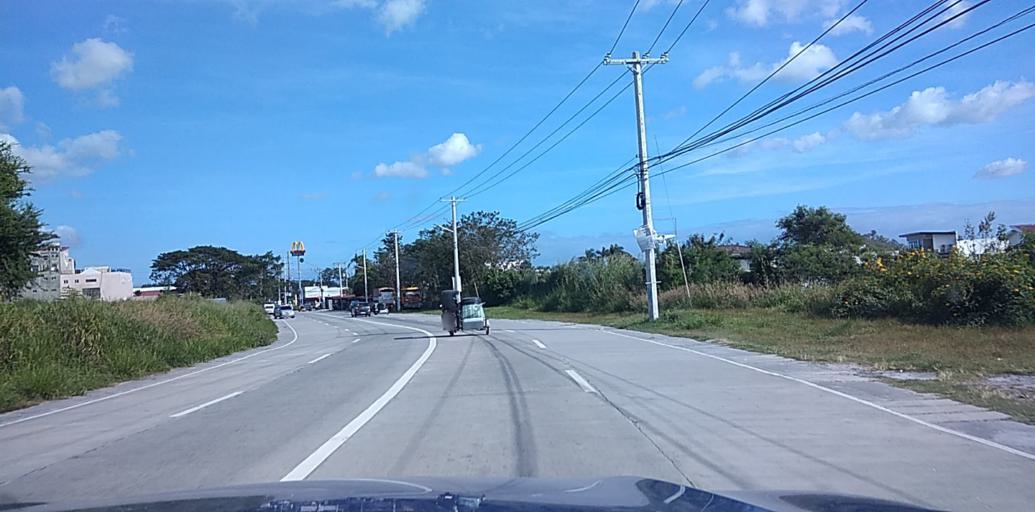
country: PH
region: Central Luzon
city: Santol
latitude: 15.1443
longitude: 120.5567
